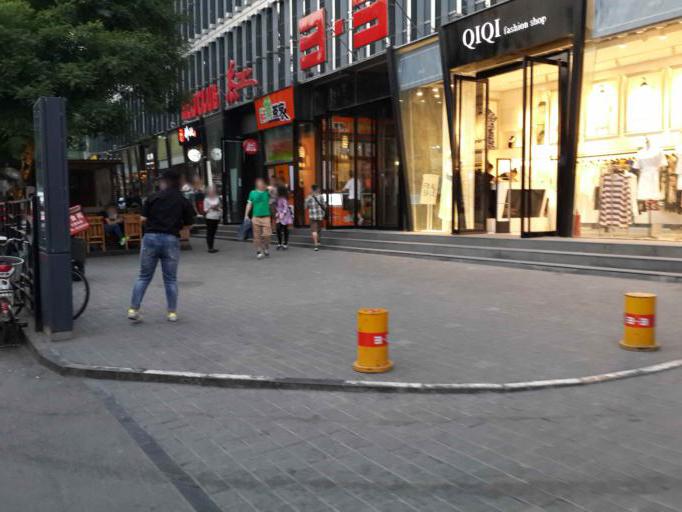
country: CN
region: Beijing
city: Chaowai
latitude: 39.9352
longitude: 116.4480
